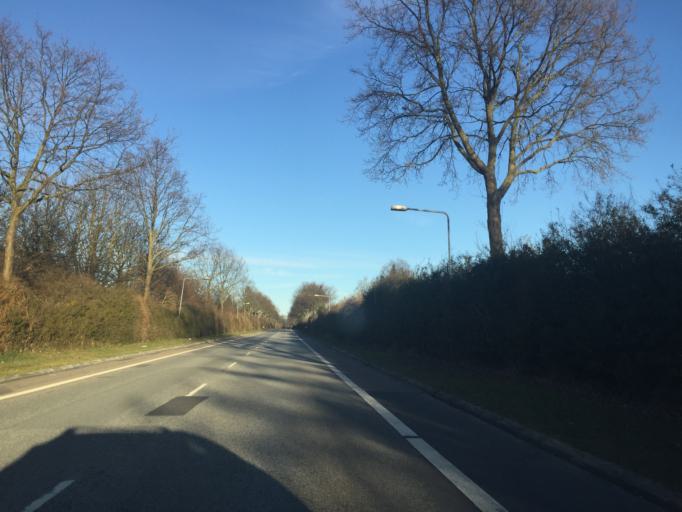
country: DK
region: Capital Region
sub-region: Dragor Kommune
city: Dragor
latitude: 55.5898
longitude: 12.6432
